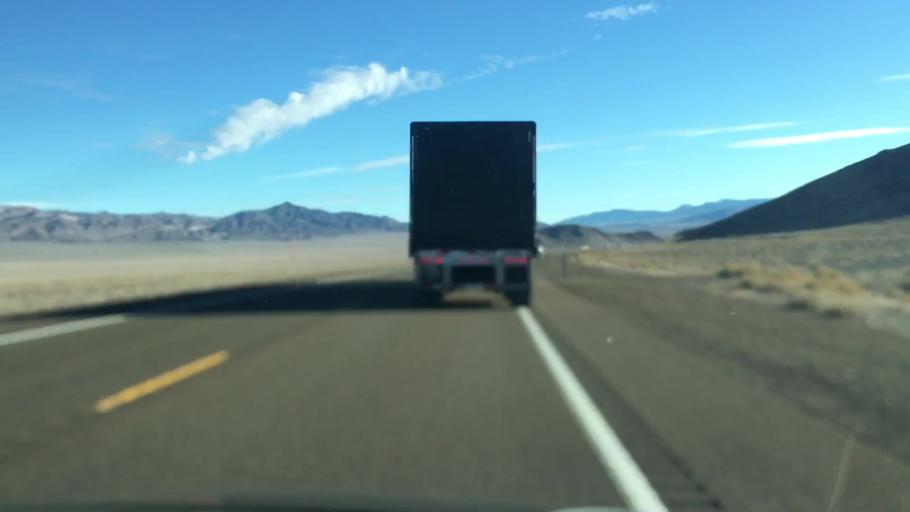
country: US
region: Nevada
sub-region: Nye County
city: Tonopah
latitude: 38.1724
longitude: -117.9589
